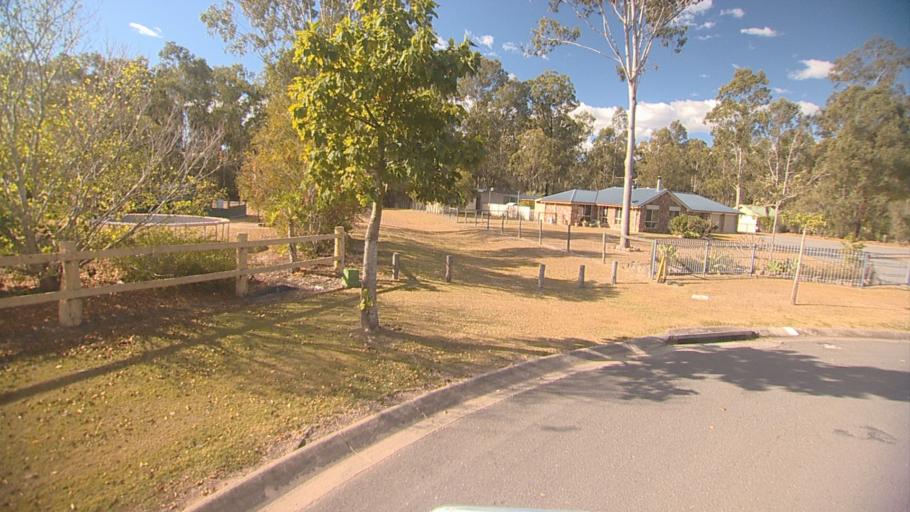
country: AU
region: Queensland
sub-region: Logan
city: North Maclean
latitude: -27.8008
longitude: 152.9705
